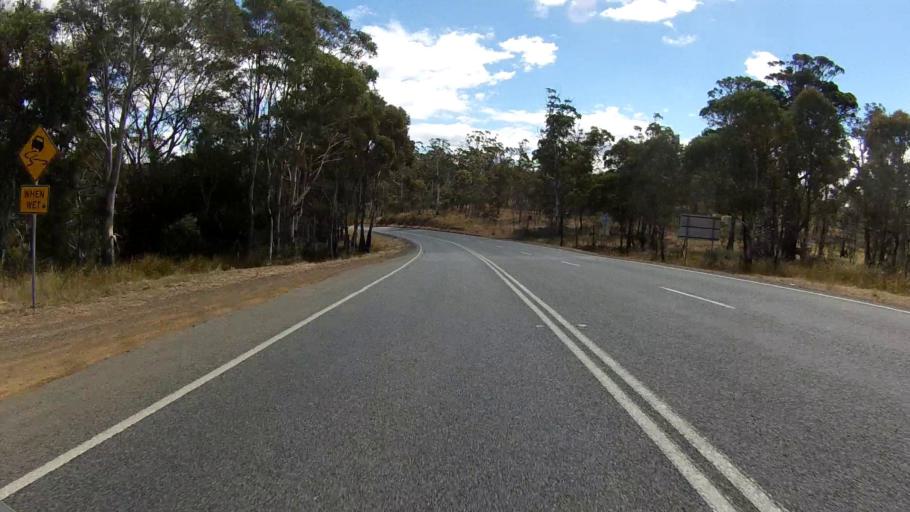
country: AU
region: Tasmania
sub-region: Sorell
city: Sorell
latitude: -42.6124
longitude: 147.6468
